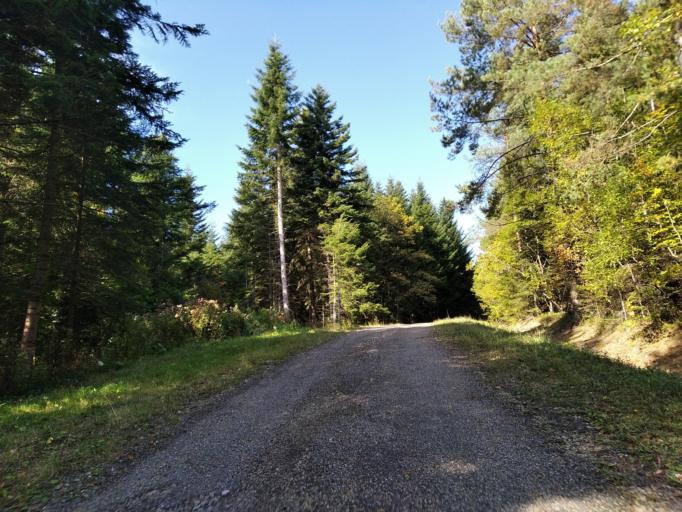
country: PL
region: Subcarpathian Voivodeship
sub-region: Powiat strzyzowski
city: Strzyzow
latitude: 49.8088
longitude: 21.8069
